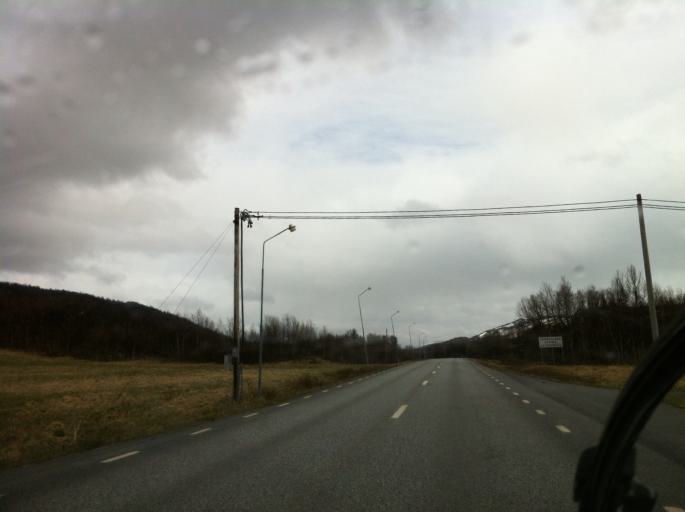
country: NO
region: Sor-Trondelag
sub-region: Tydal
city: Aas
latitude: 62.5889
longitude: 12.1942
